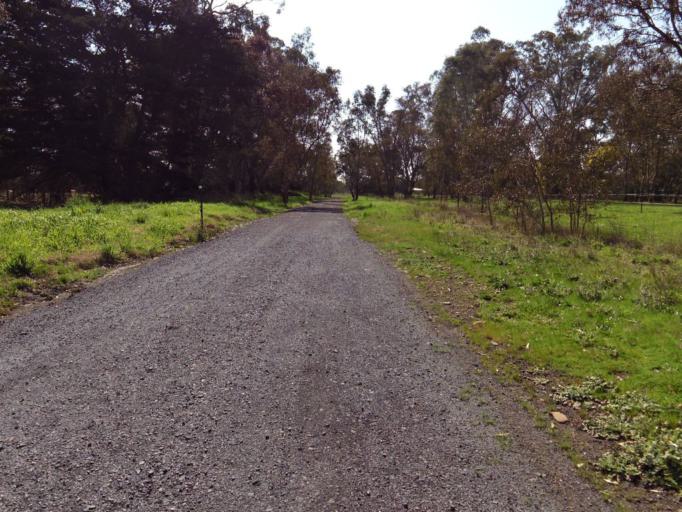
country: AU
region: Victoria
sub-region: Murrindindi
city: Alexandra
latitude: -37.1061
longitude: 145.6155
